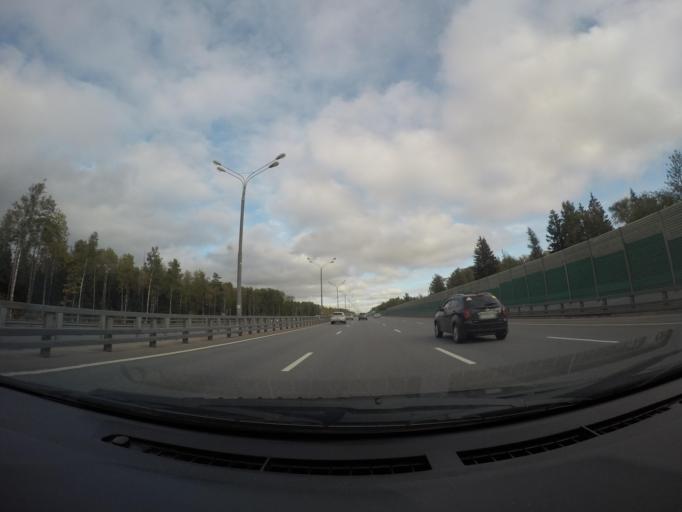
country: RU
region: Moskovskaya
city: Krasnoznamensk
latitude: 55.6064
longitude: 37.0346
